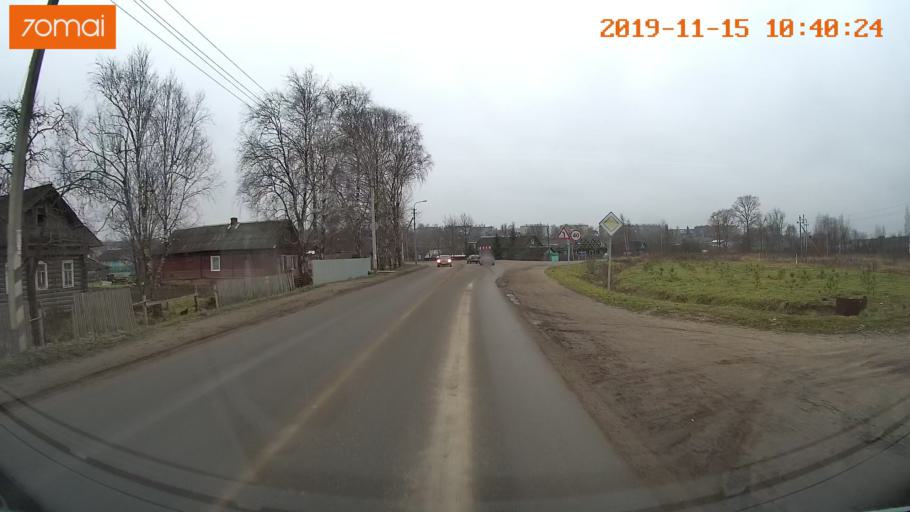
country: RU
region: Vologda
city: Sheksna
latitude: 59.2147
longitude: 38.5093
